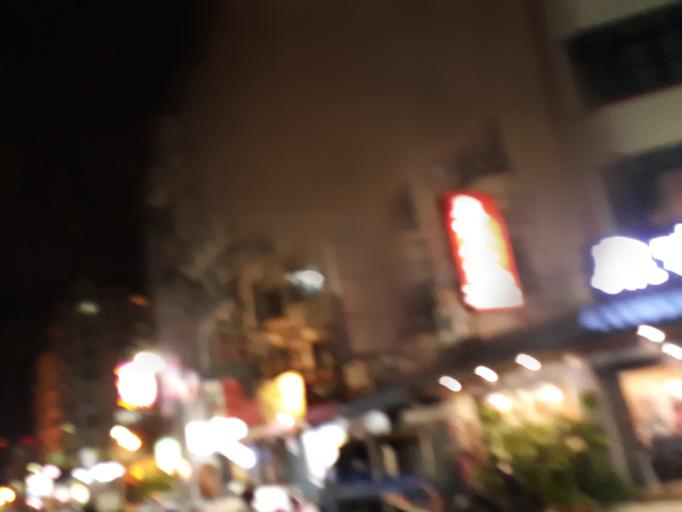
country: TW
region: Taiwan
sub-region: Hsinchu
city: Hsinchu
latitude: 24.8155
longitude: 120.9769
